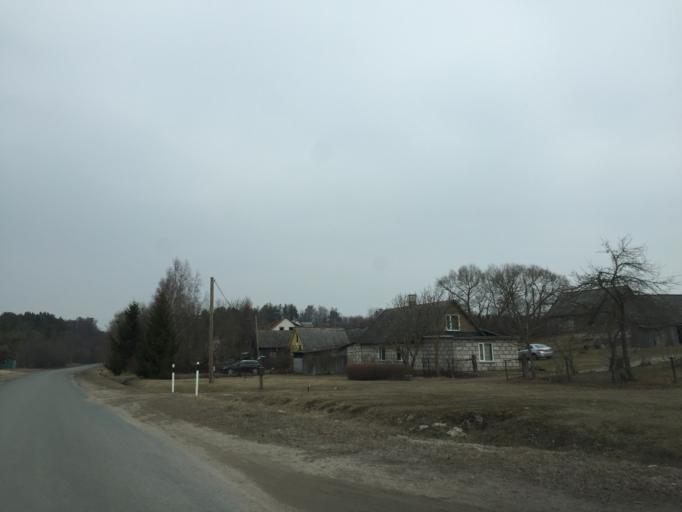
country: LV
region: Salacgrivas
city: Ainazi
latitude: 58.0132
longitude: 24.4498
